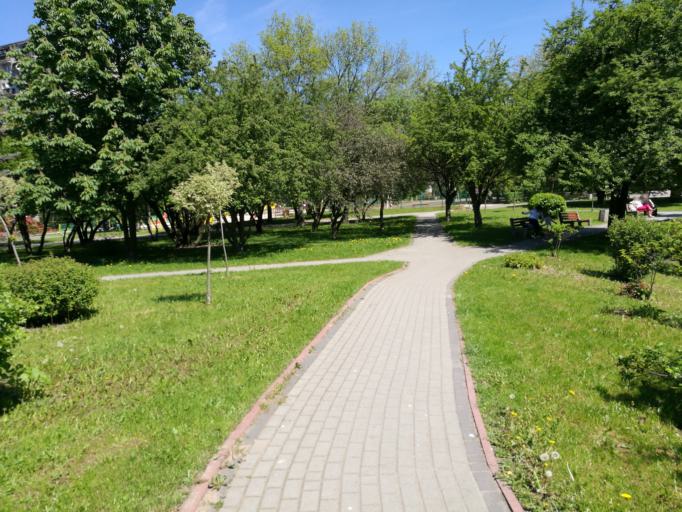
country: PL
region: Swietokrzyskie
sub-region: Powiat kielecki
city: Kielce
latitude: 50.8643
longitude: 20.6420
